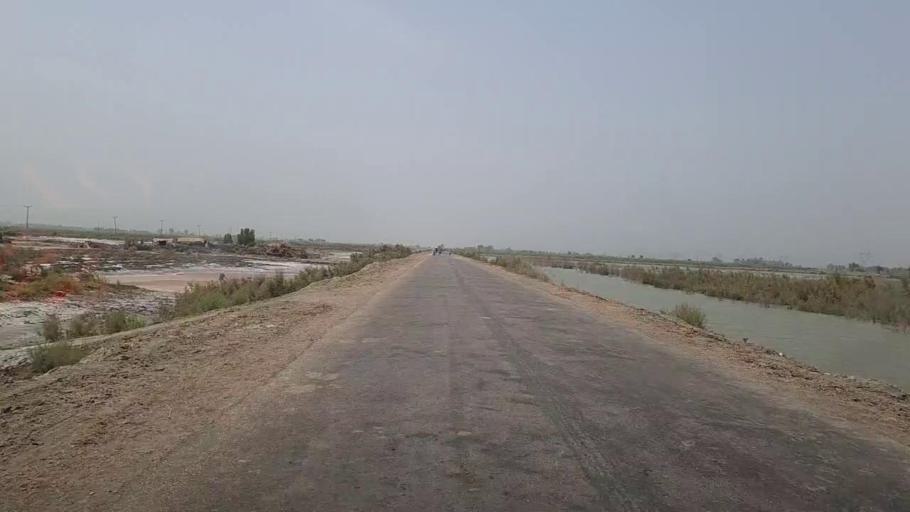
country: PK
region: Sindh
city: Radhan
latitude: 27.1581
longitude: 67.9415
